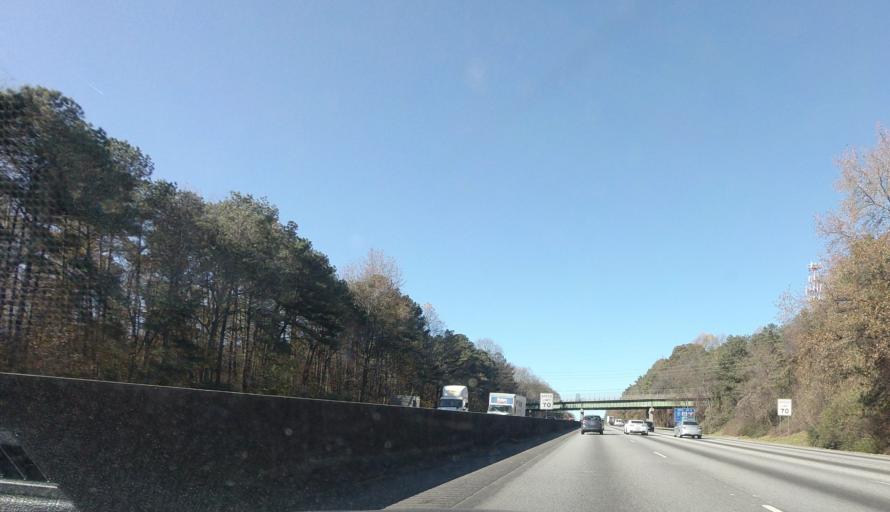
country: US
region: Georgia
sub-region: Cobb County
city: Mableton
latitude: 33.7750
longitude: -84.5770
